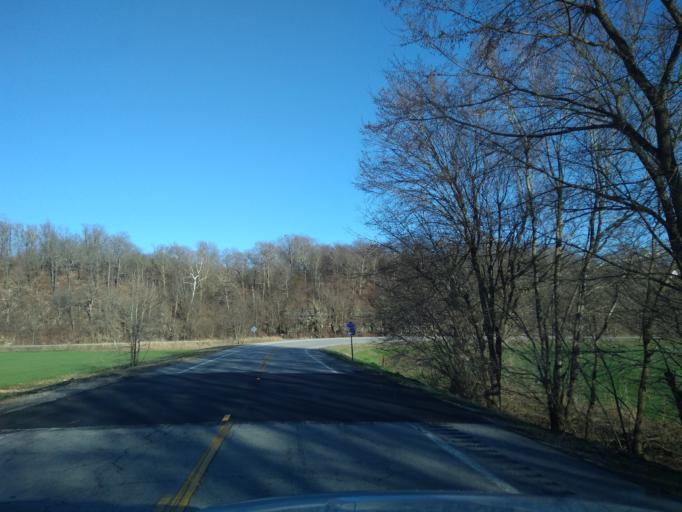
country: US
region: Arkansas
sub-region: Washington County
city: Farmington
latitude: 36.1029
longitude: -94.3428
